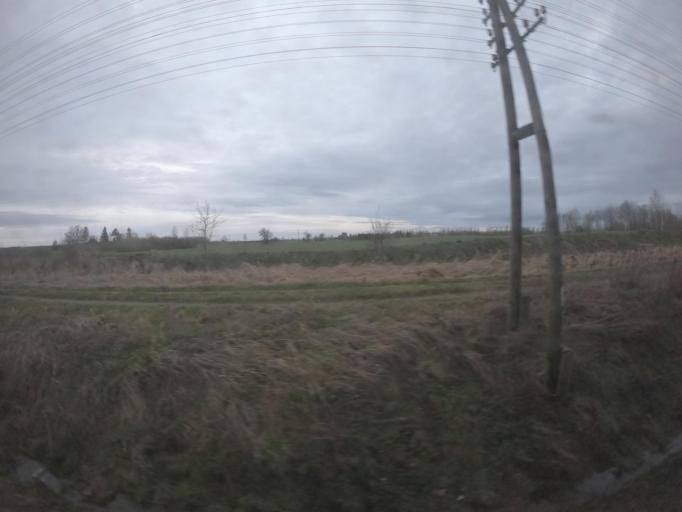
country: PL
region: West Pomeranian Voivodeship
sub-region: Powiat szczecinecki
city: Borne Sulinowo
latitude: 53.6274
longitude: 16.4757
